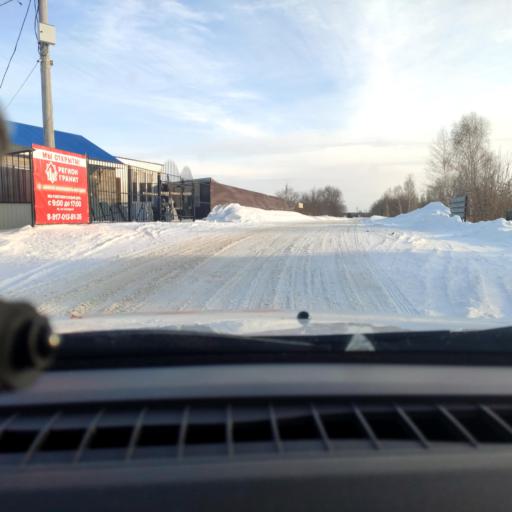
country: RU
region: Samara
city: Chapayevsk
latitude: 52.9927
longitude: 49.7416
